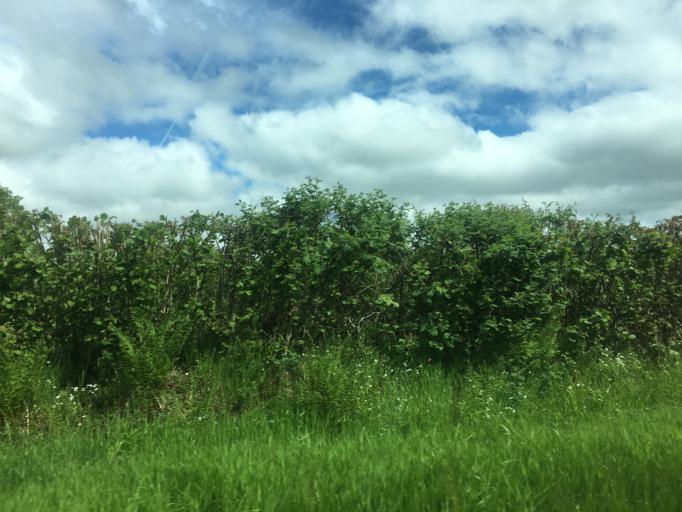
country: GB
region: Wales
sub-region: Carmarthenshire
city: Llansawel
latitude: 52.0636
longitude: -3.9742
